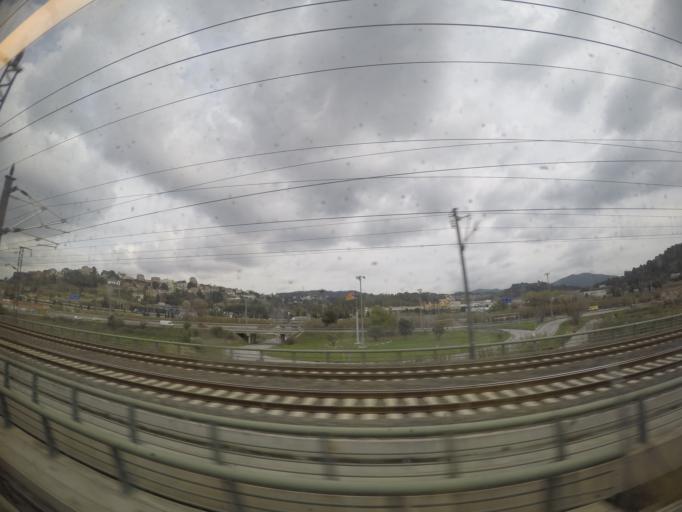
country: ES
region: Catalonia
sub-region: Provincia de Barcelona
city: Palleja
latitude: 41.4311
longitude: 2.0022
